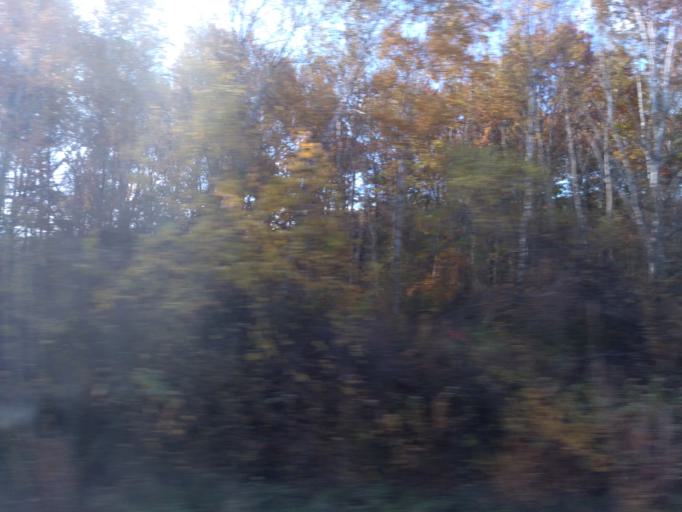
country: JP
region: Hokkaido
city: Kitahiroshima
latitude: 42.9644
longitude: 141.5680
